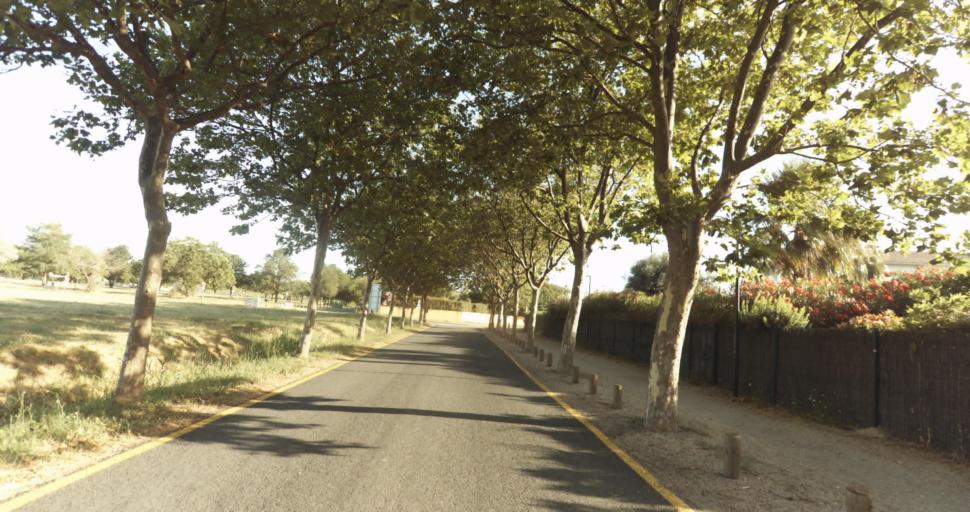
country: FR
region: Languedoc-Roussillon
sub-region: Departement des Pyrenees-Orientales
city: Latour-Bas-Elne
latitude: 42.6006
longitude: 3.0325
